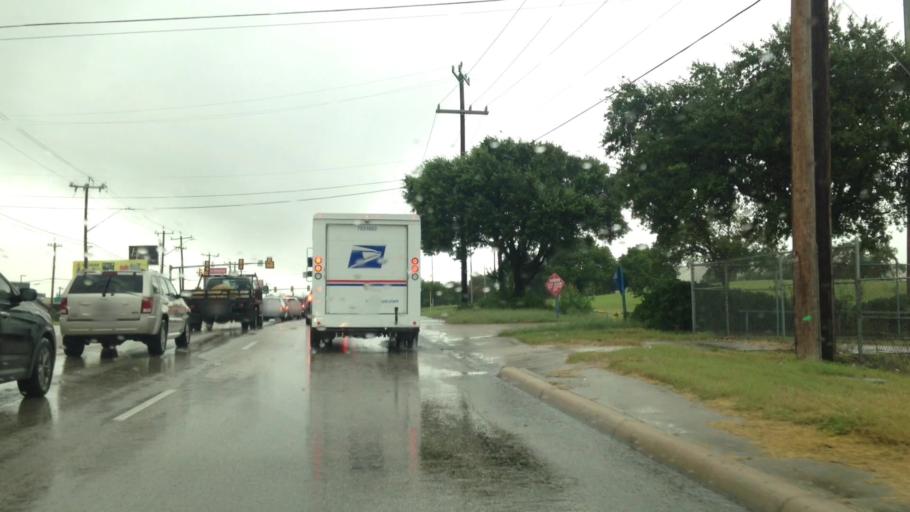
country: US
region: Texas
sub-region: Bexar County
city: Windcrest
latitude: 29.5309
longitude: -98.4110
